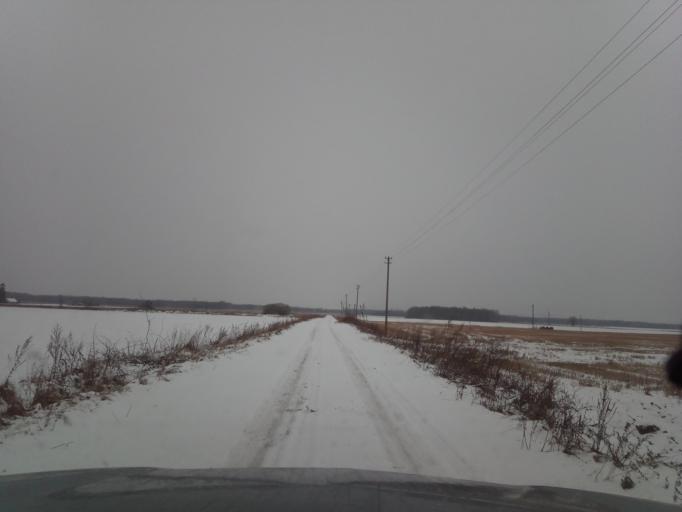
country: LT
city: Ramygala
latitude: 55.6191
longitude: 24.3461
